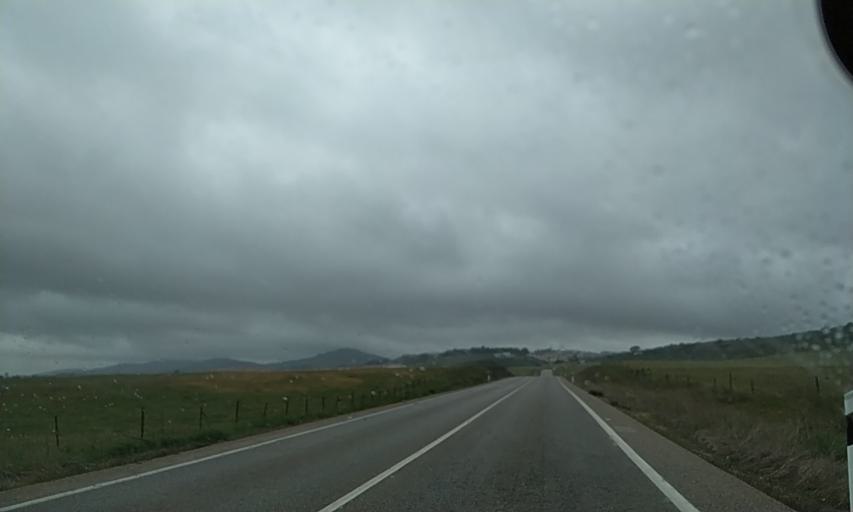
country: ES
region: Extremadura
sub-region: Provincia de Caceres
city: Caceres
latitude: 39.5001
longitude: -6.3883
